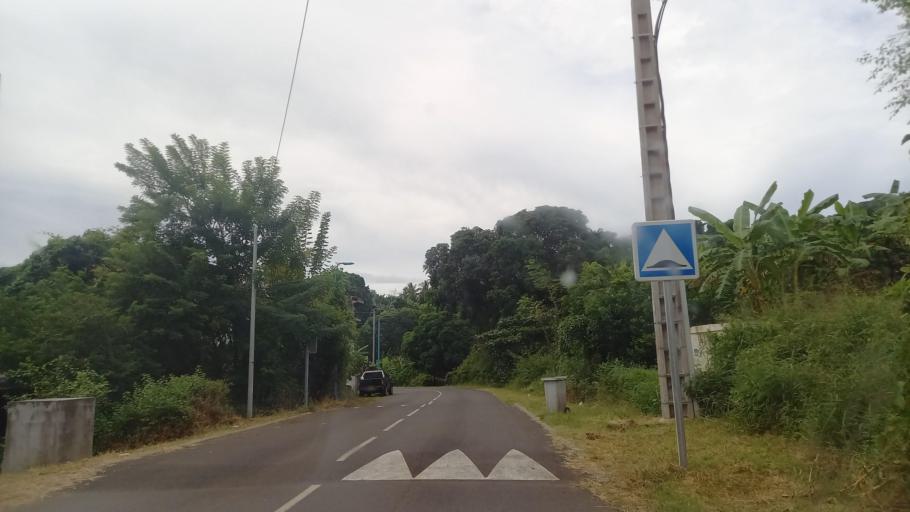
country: YT
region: Kani-Keli
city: Kani Keli
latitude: -12.9441
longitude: 45.1024
